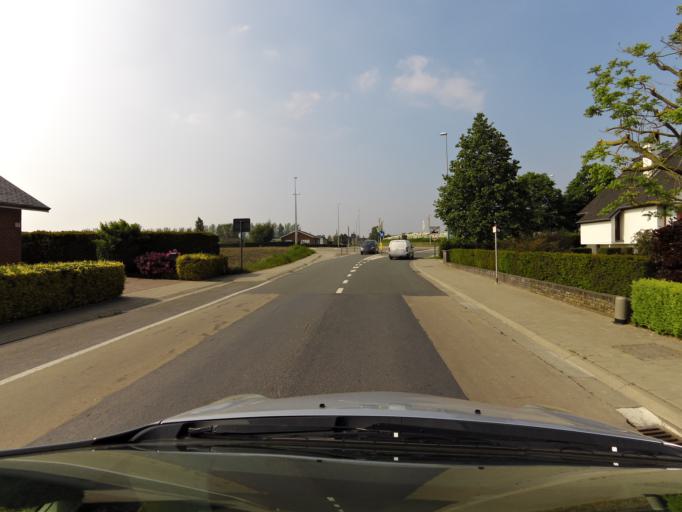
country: BE
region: Flanders
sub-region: Provincie West-Vlaanderen
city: Poperinge
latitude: 50.8636
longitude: 2.7180
